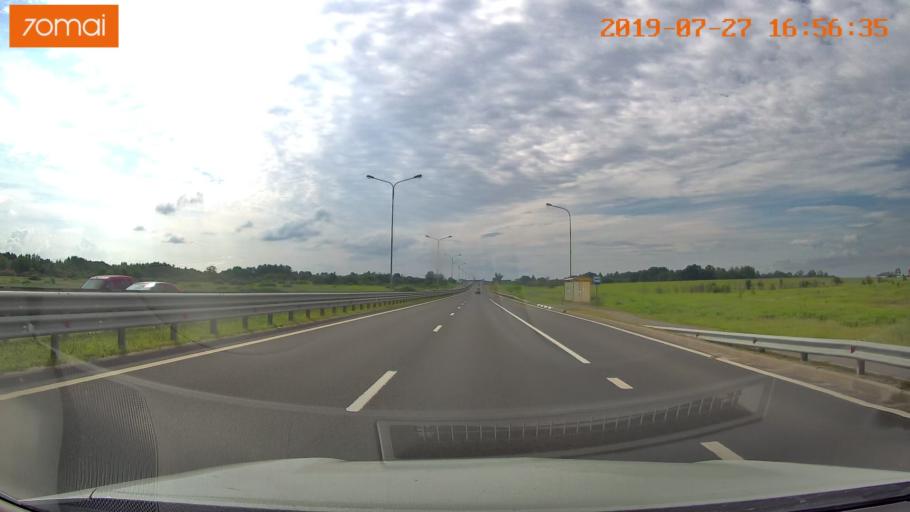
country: RU
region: Kaliningrad
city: Bol'shoe Isakovo
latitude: 54.6955
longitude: 20.7351
